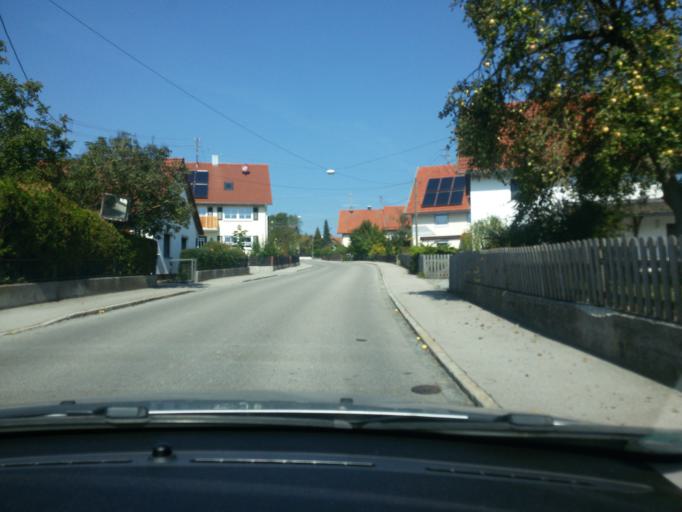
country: DE
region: Bavaria
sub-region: Swabia
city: Scherstetten
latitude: 48.2034
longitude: 10.6508
